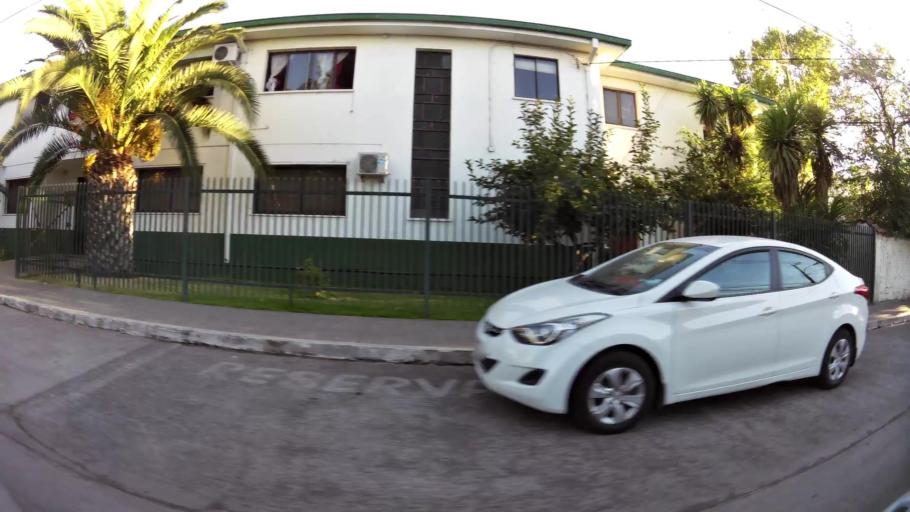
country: CL
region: Maule
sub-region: Provincia de Curico
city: Curico
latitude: -34.9897
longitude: -71.2426
